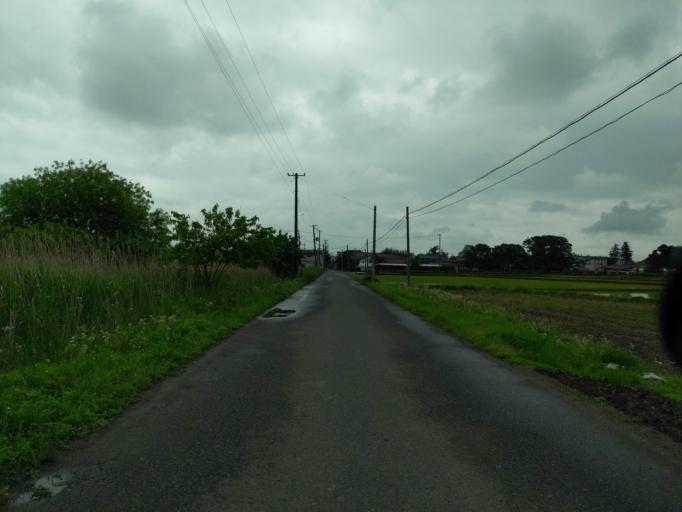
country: JP
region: Fukushima
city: Koriyama
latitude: 37.3647
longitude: 140.3201
